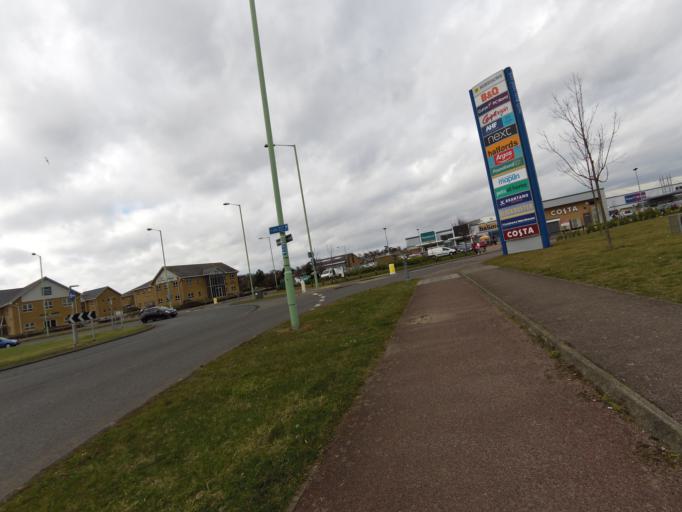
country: GB
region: England
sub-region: Suffolk
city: Lowestoft
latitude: 52.4770
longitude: 1.7329
